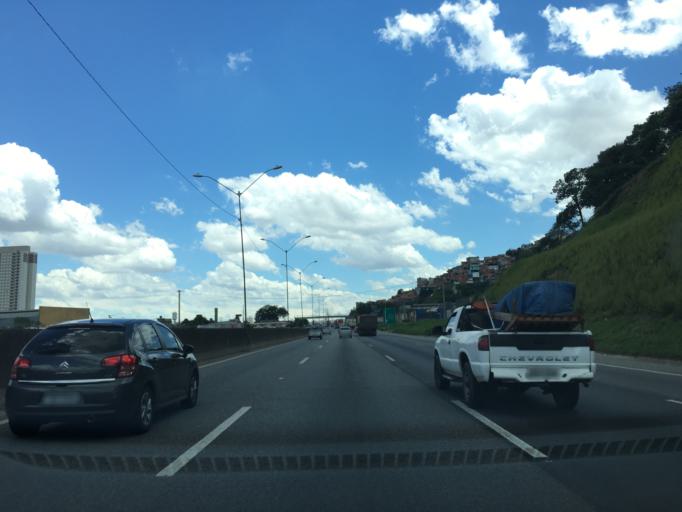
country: BR
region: Sao Paulo
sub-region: Guarulhos
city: Guarulhos
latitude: -23.4450
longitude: -46.5687
